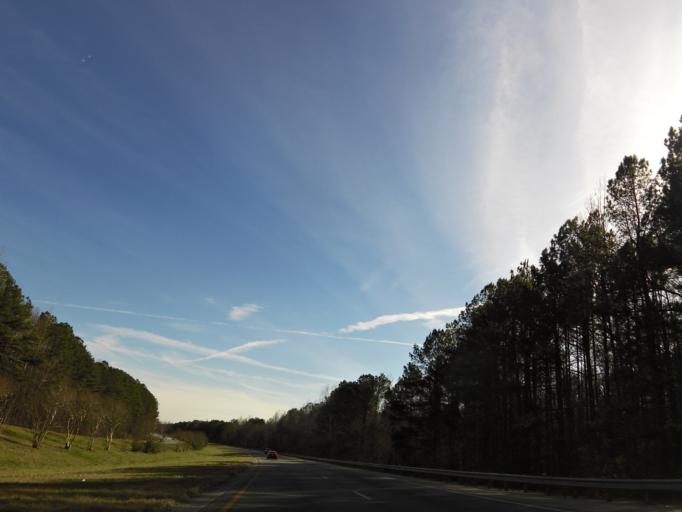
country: US
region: Georgia
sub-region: Harris County
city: Hamilton
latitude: 32.7208
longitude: -85.0192
